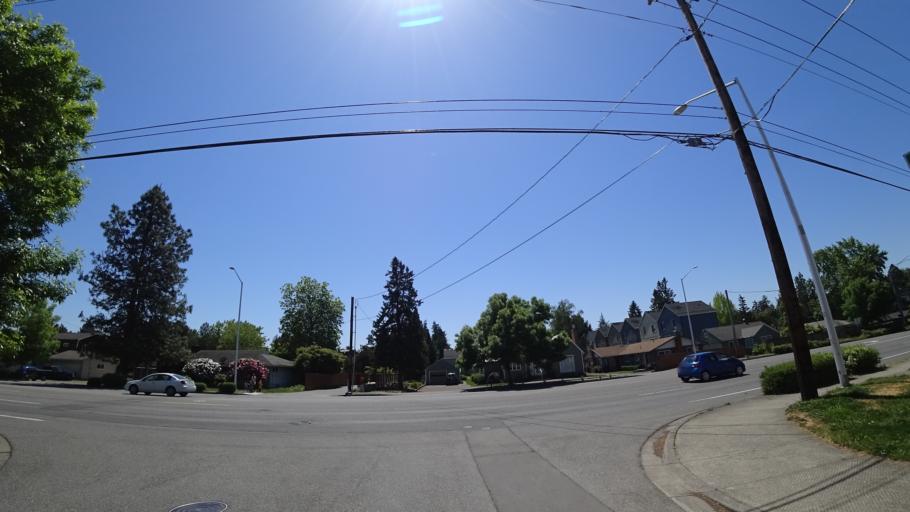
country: US
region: Oregon
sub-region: Washington County
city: Beaverton
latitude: 45.4857
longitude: -122.8289
